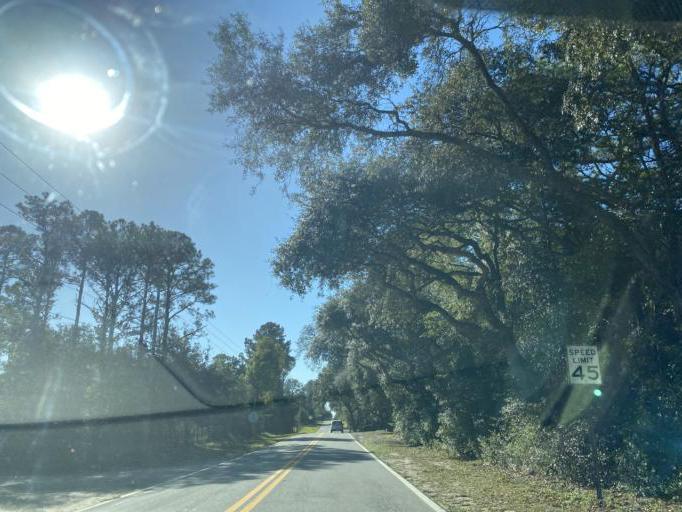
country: US
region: Florida
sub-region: Orange County
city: Tangerine
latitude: 28.7986
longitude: -81.5928
